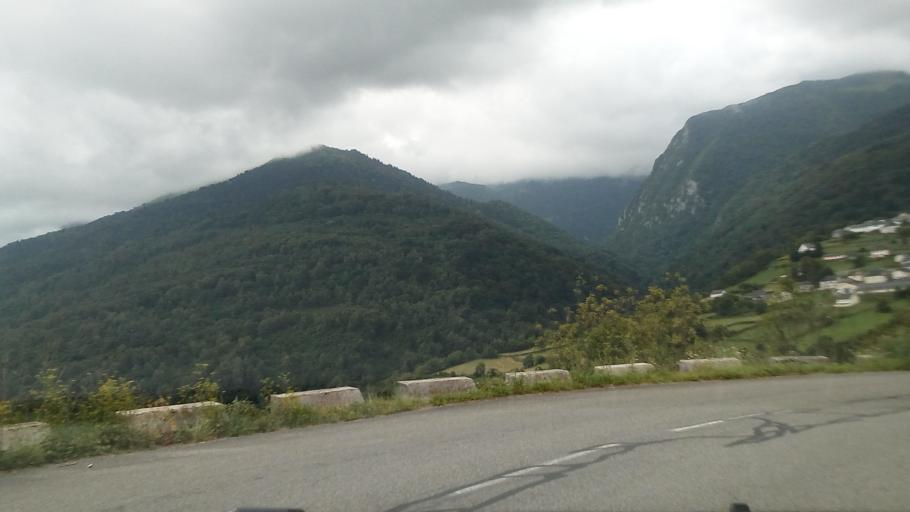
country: FR
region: Aquitaine
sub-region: Departement des Pyrenees-Atlantiques
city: Louvie-Juzon
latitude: 43.0625
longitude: -0.4404
